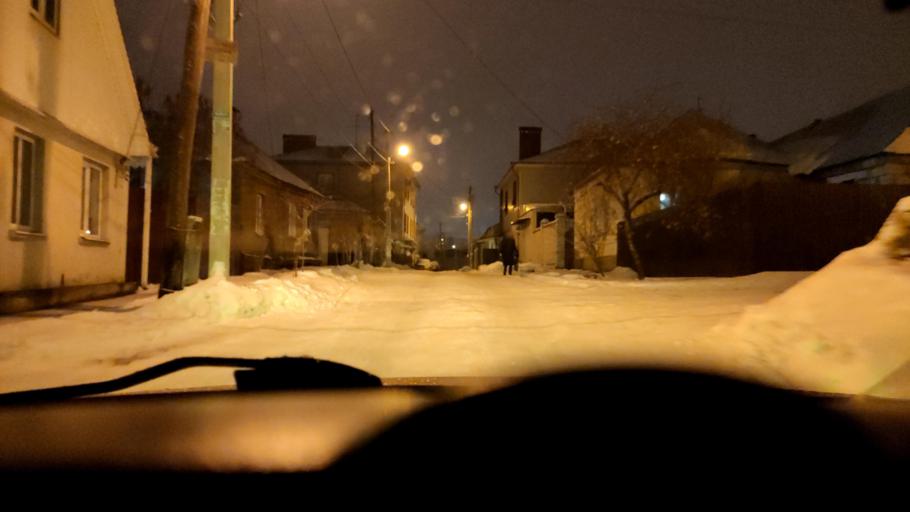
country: RU
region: Voronezj
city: Voronezh
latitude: 51.6303
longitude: 39.2000
